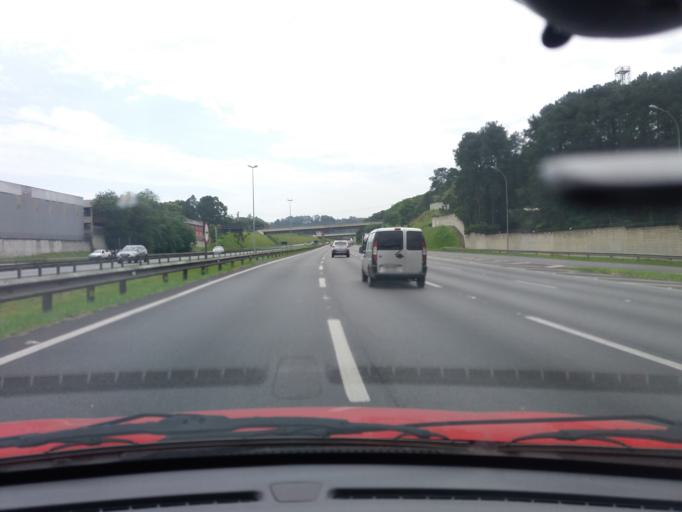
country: BR
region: Sao Paulo
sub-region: Carapicuiba
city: Carapicuiba
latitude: -23.5073
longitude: -46.8217
